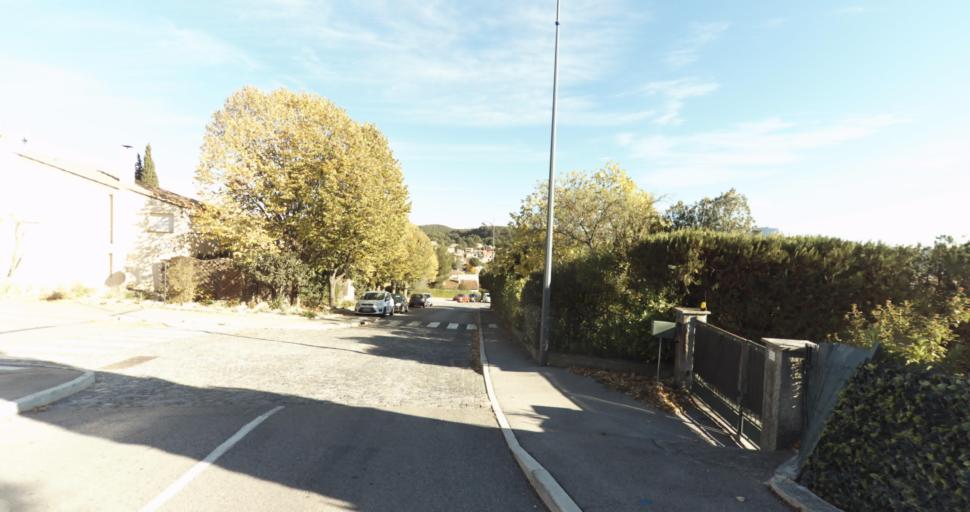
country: FR
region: Provence-Alpes-Cote d'Azur
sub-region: Departement des Bouches-du-Rhone
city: Venelles
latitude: 43.5990
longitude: 5.4824
